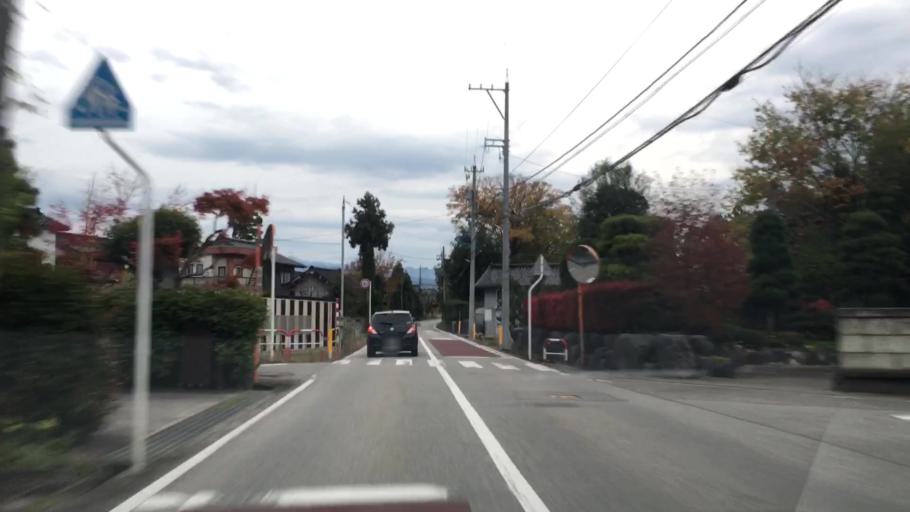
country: JP
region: Toyama
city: Kamiichi
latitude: 36.6940
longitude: 137.3152
